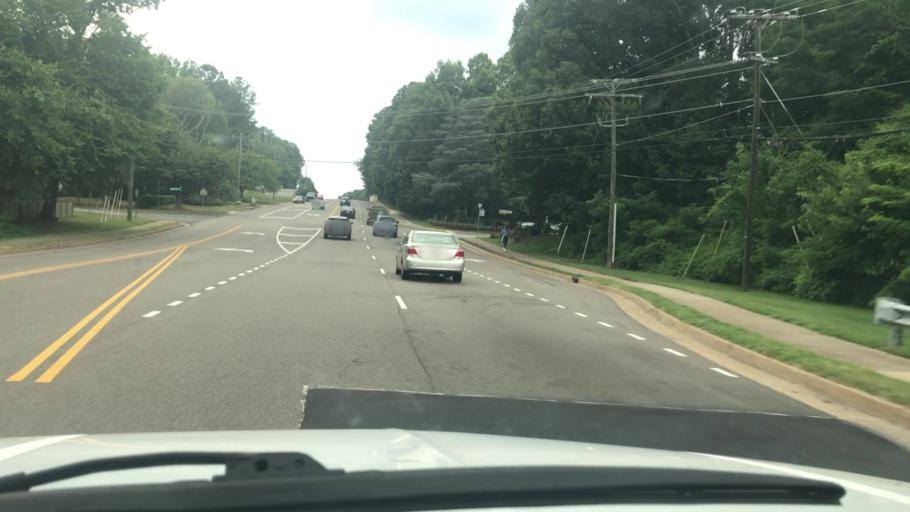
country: US
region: Virginia
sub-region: Henrico County
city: Tuckahoe
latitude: 37.6074
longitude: -77.5849
